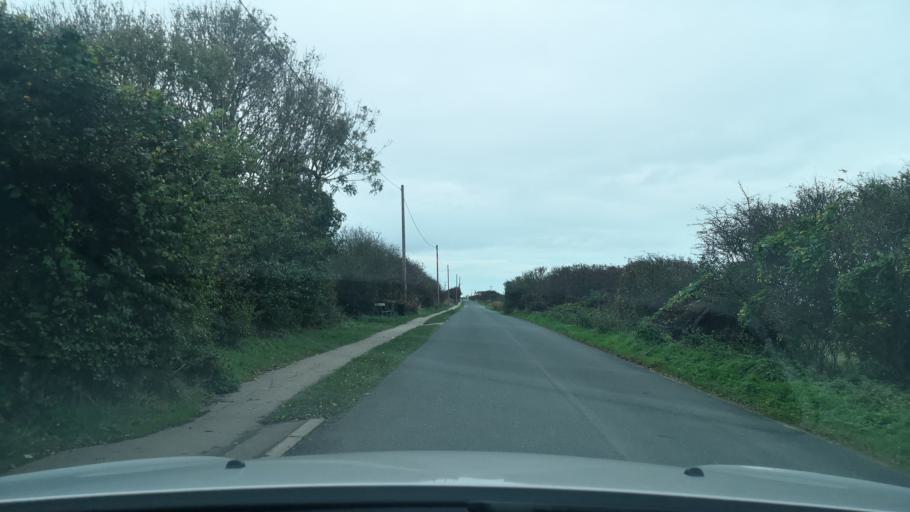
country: GB
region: England
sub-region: East Riding of Yorkshire
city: Easington
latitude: 53.6198
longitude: 0.1318
